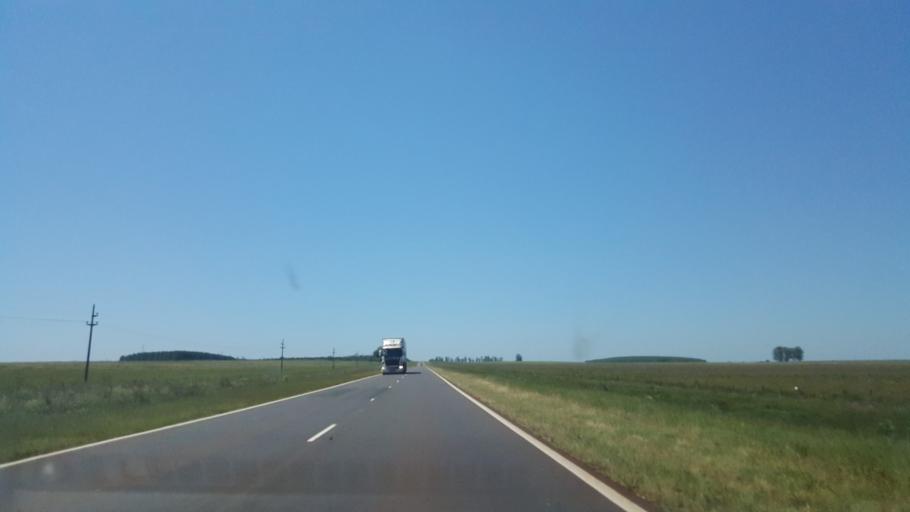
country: AR
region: Corrientes
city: Santo Tome
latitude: -28.4033
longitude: -56.1077
